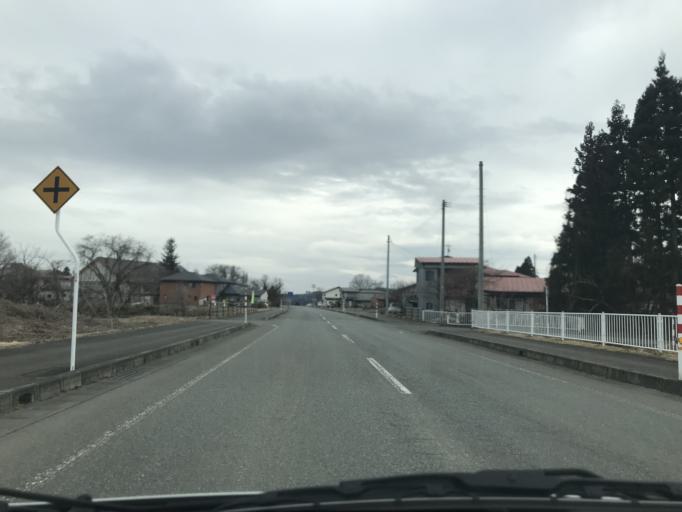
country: JP
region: Iwate
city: Kitakami
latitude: 39.3138
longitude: 140.9756
